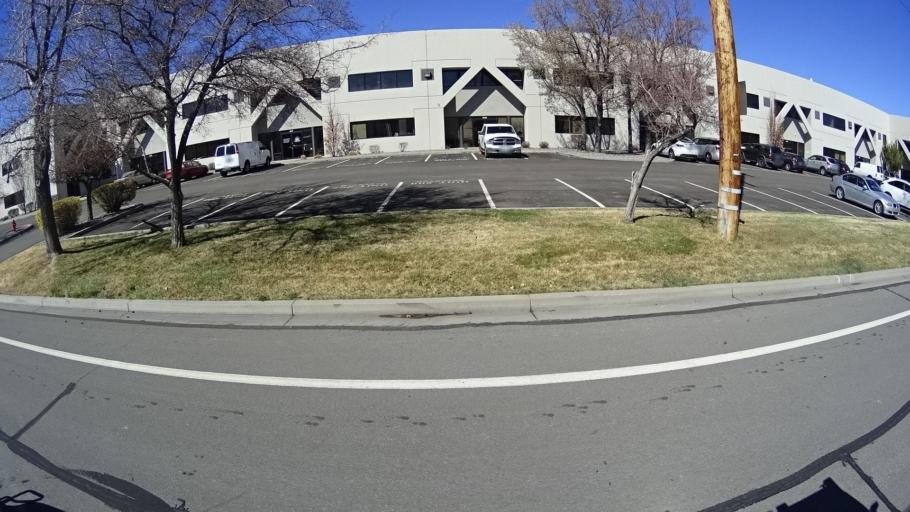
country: US
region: Nevada
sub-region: Washoe County
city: Sparks
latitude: 39.4855
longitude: -119.7589
